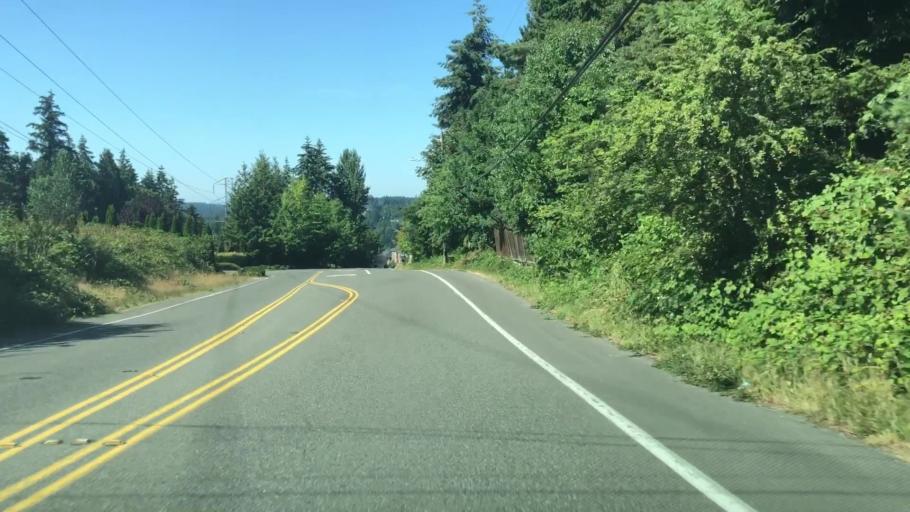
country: US
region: Washington
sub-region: King County
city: Woodinville
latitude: 47.7492
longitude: -122.1745
